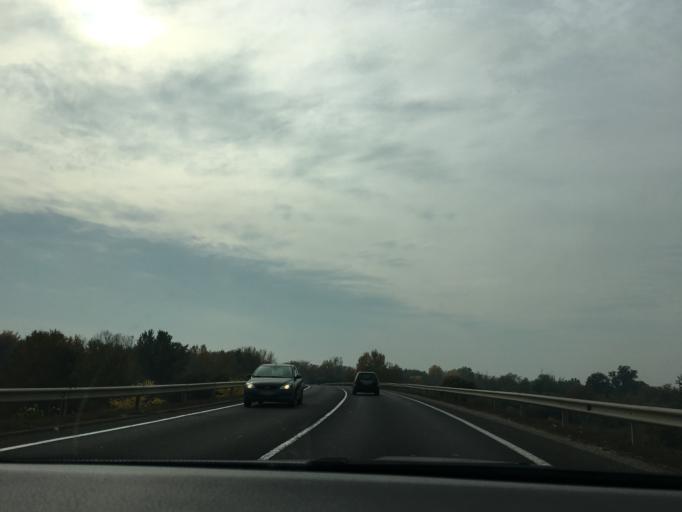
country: HU
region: Hajdu-Bihar
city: Debrecen
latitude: 47.5086
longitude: 21.5950
